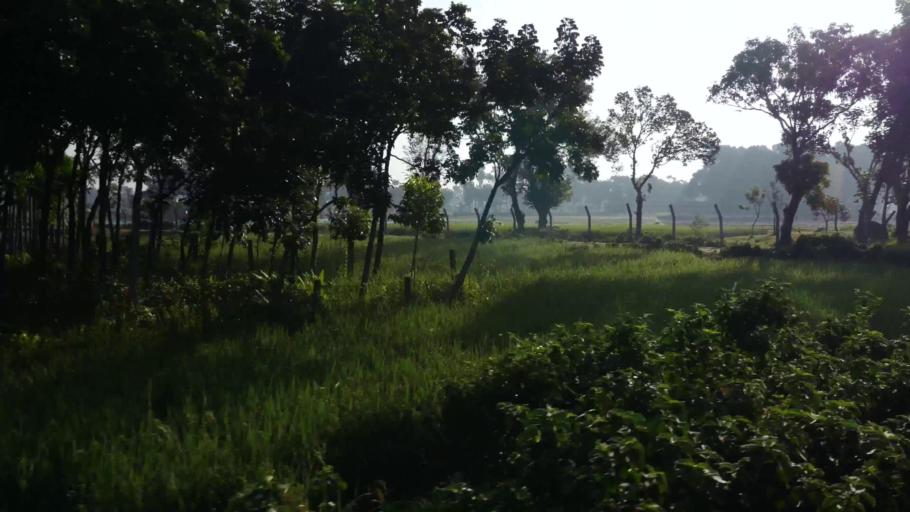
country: BD
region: Dhaka
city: Jamalpur
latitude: 24.9126
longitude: 89.9592
